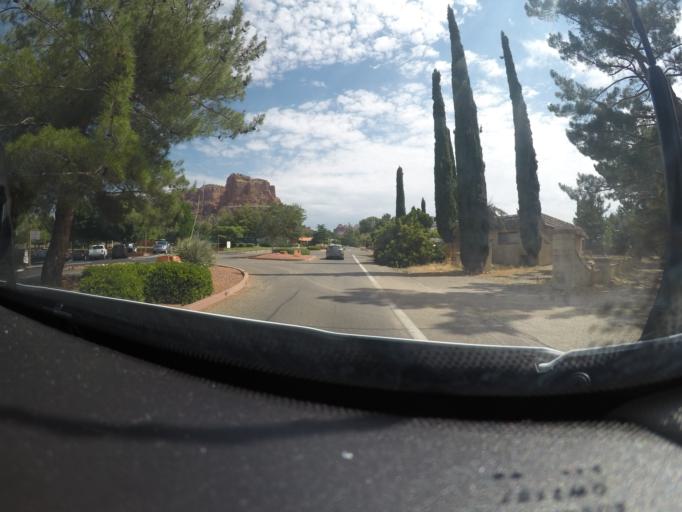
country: US
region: Arizona
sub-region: Yavapai County
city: Big Park
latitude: 34.7817
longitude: -111.7743
